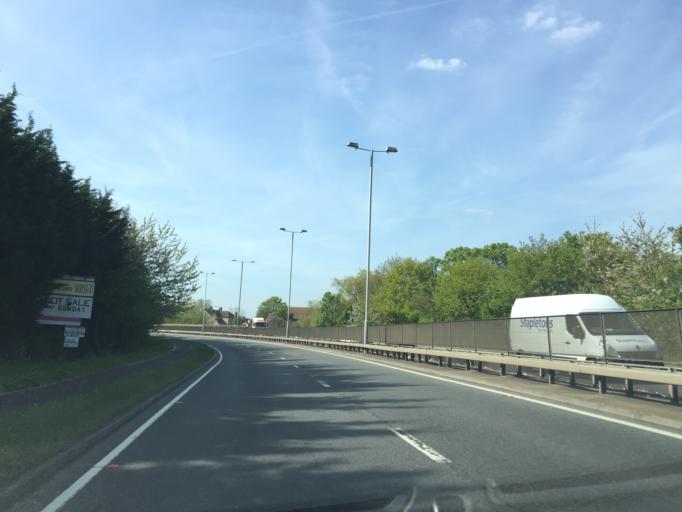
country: GB
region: England
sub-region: Greater London
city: Sidcup
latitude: 51.4290
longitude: 0.0843
